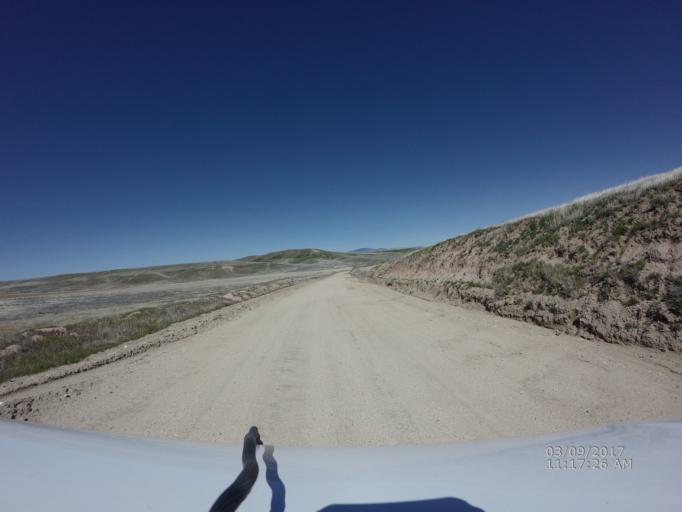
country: US
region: California
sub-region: Los Angeles County
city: Green Valley
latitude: 34.7106
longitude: -118.4000
